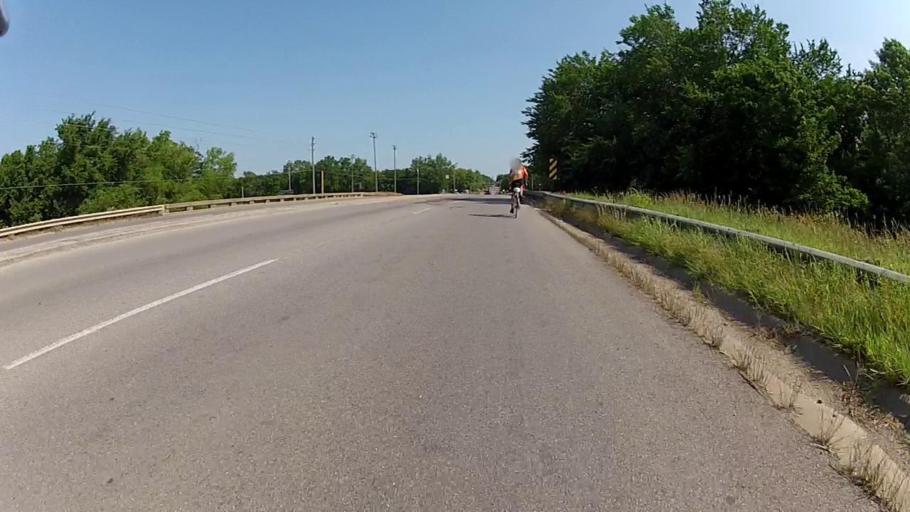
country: US
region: Kansas
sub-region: Montgomery County
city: Independence
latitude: 37.2140
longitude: -95.7108
